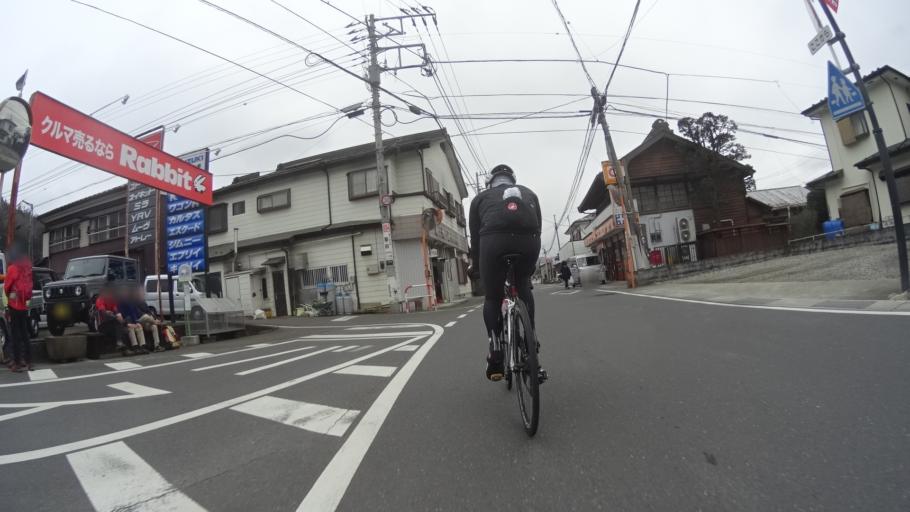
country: JP
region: Yamanashi
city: Uenohara
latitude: 35.6391
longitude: 139.1054
